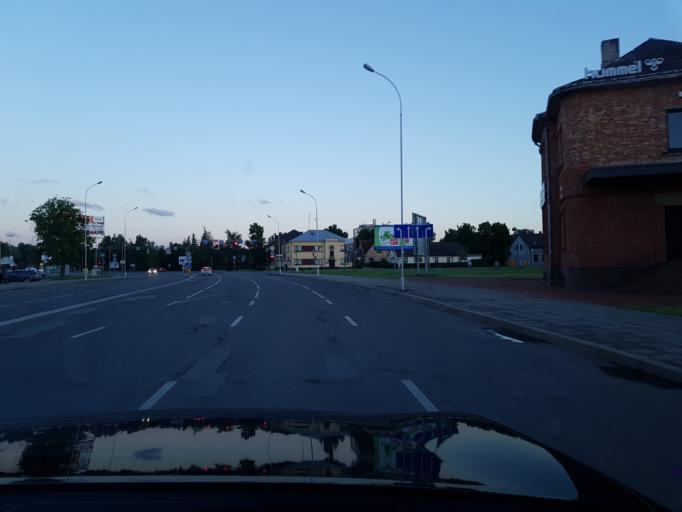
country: LT
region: Marijampoles apskritis
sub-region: Marijampole Municipality
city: Marijampole
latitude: 54.5617
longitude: 23.3532
